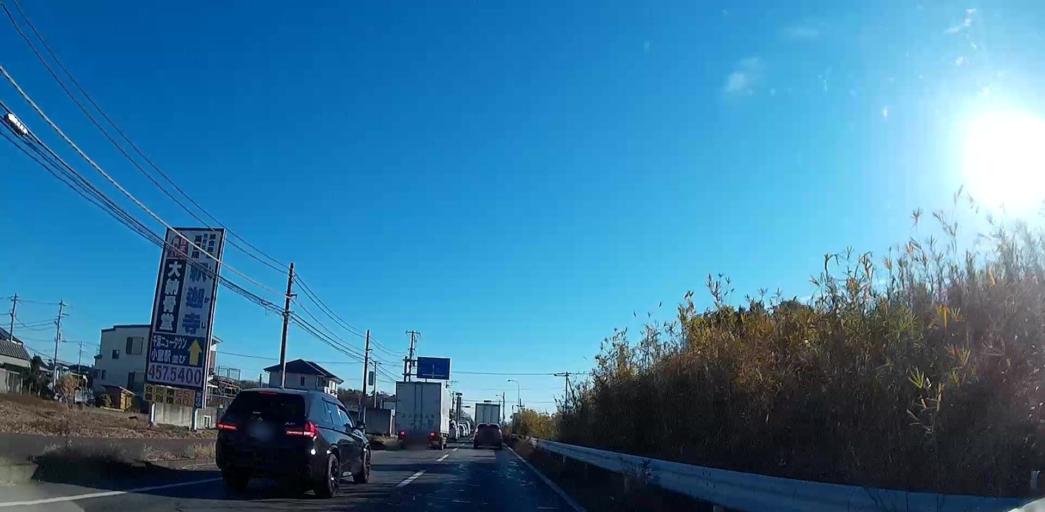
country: JP
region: Chiba
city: Shiroi
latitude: 35.7845
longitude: 140.0147
